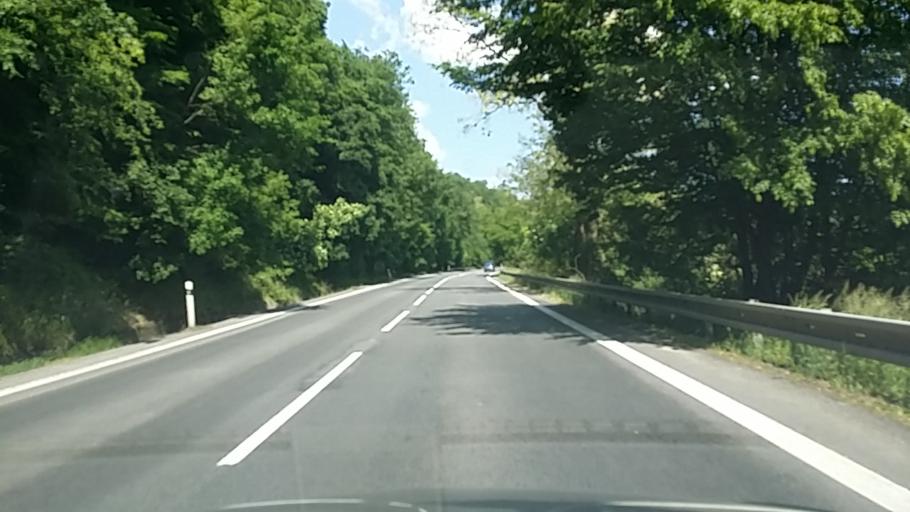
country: SK
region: Banskobystricky
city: Krupina
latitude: 48.2687
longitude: 18.9907
